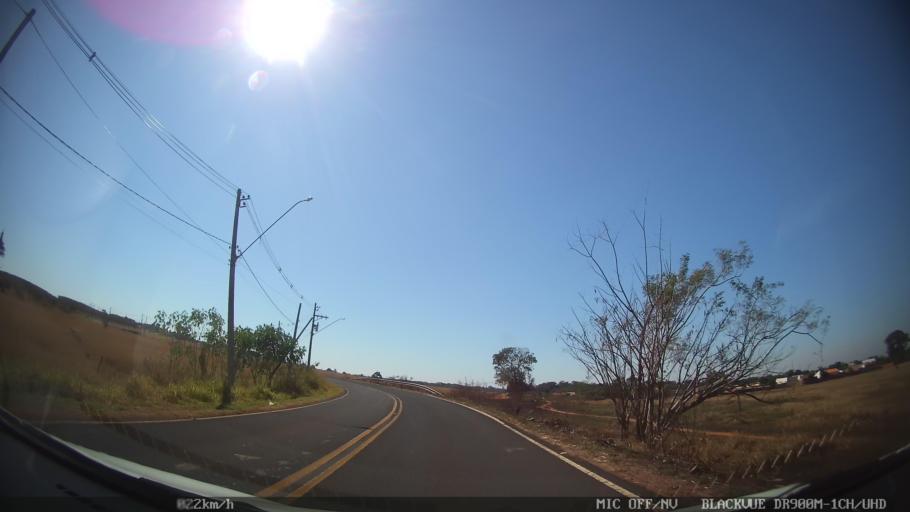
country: BR
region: Sao Paulo
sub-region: Sao Jose Do Rio Preto
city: Sao Jose do Rio Preto
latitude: -20.7451
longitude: -49.4344
